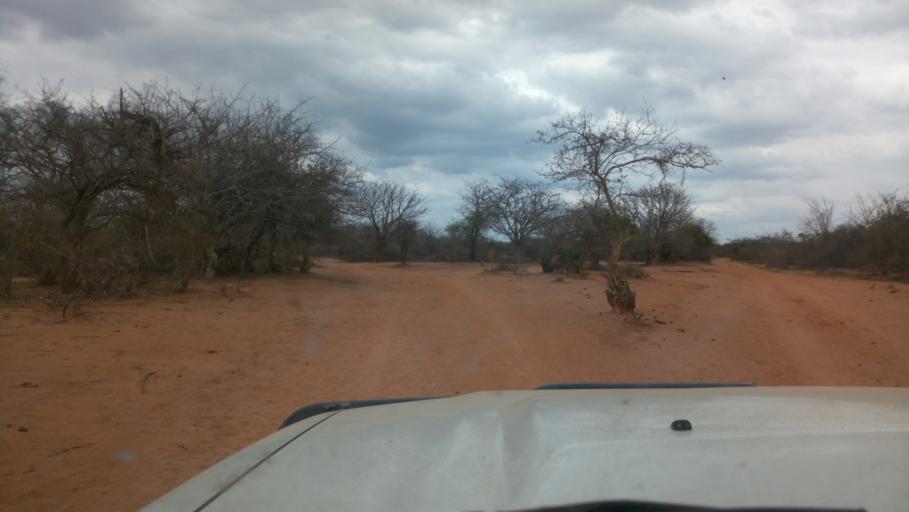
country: KE
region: Kitui
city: Kitui
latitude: -1.8445
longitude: 38.4558
